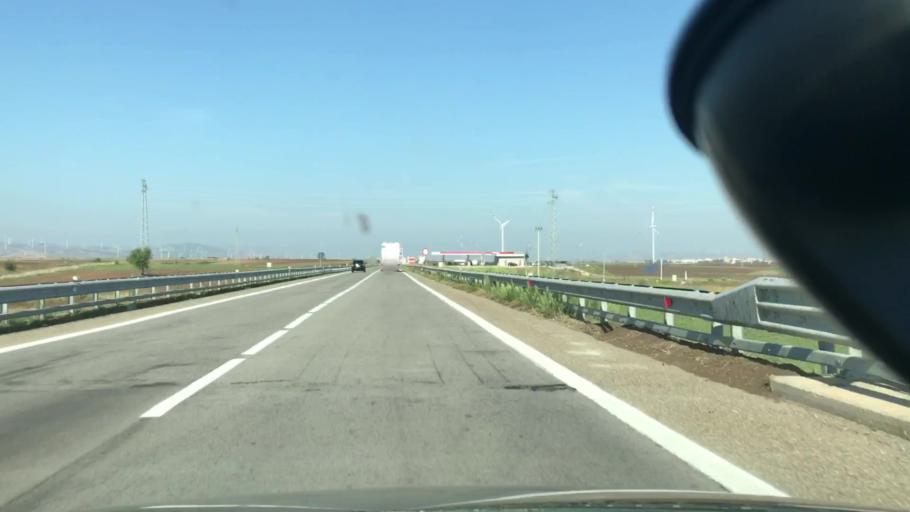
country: IT
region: Basilicate
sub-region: Provincia di Potenza
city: Lavello
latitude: 41.0163
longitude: 15.8194
